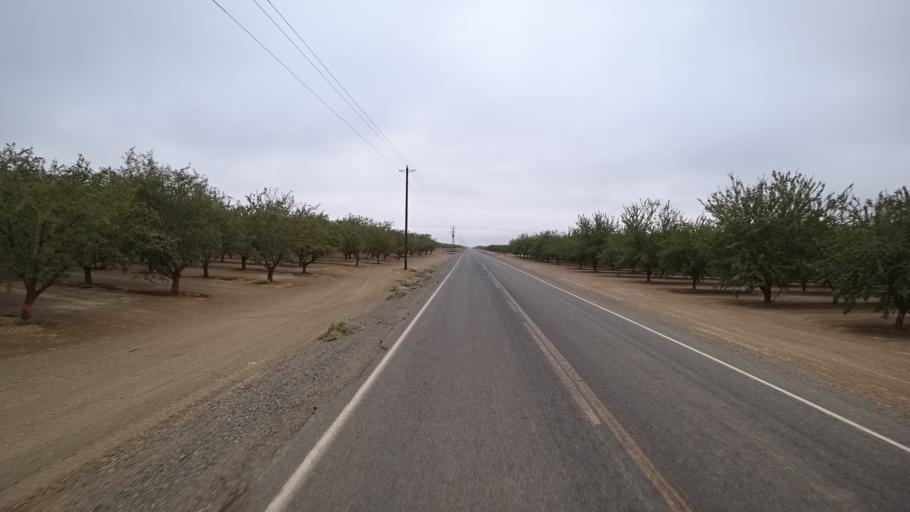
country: US
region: California
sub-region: Yolo County
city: Dunnigan
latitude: 38.9255
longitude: -121.9719
